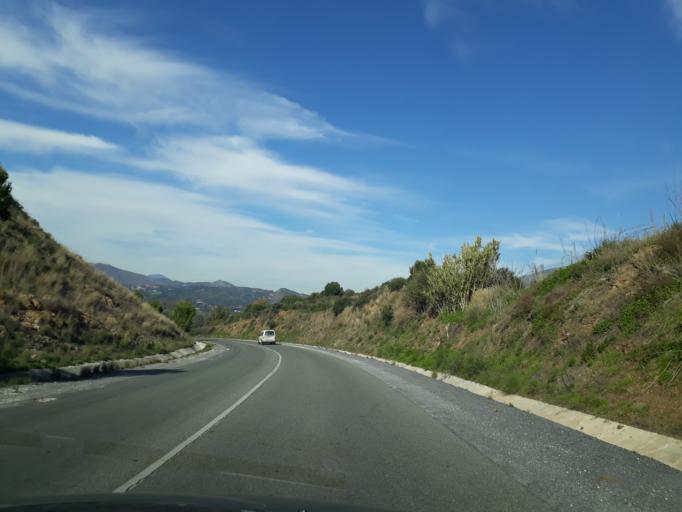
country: ES
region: Andalusia
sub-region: Provincia de Malaga
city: Fuengirola
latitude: 36.5361
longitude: -4.6860
